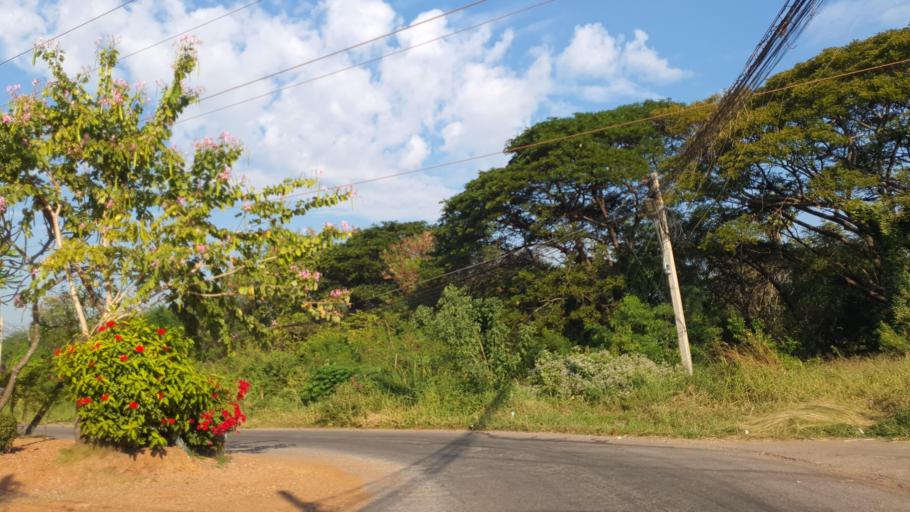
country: TH
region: Khon Kaen
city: Khon Kaen
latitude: 16.4123
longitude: 102.8075
